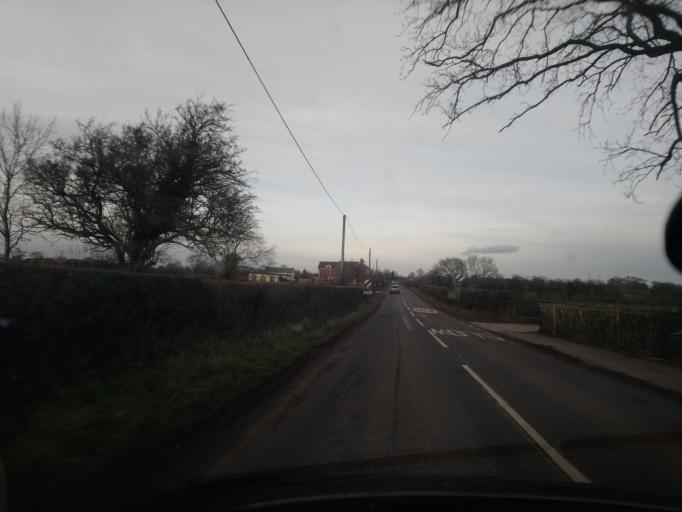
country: GB
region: England
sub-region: Shropshire
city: Wem
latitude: 52.8953
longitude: -2.7086
